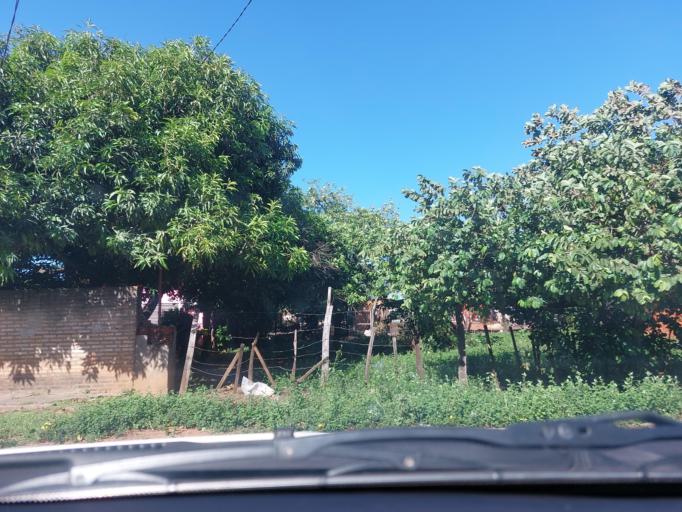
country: PY
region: San Pedro
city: Guayaybi
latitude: -24.6572
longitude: -56.4497
